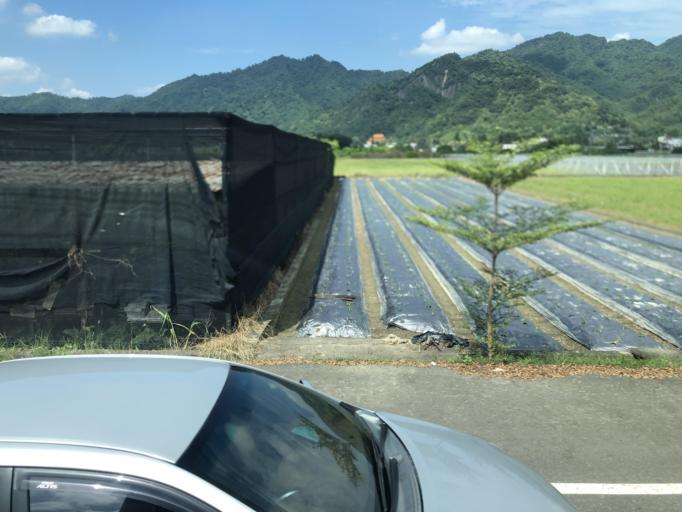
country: TW
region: Taiwan
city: Yujing
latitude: 22.9094
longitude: 120.5607
